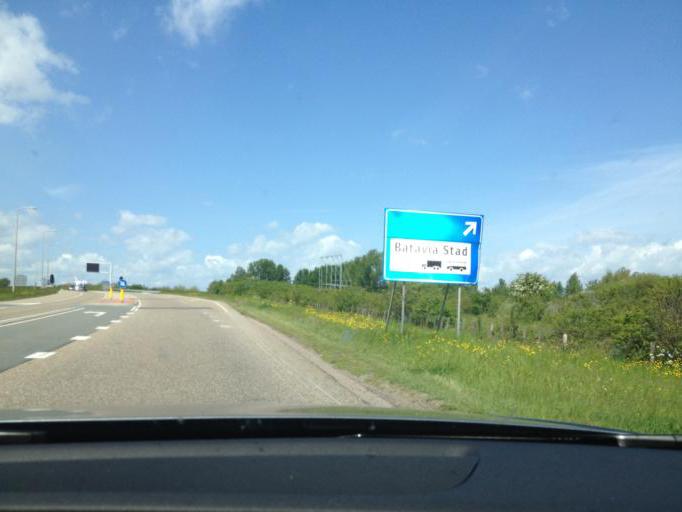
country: NL
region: Flevoland
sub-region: Gemeente Lelystad
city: Lelystad
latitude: 52.5266
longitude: 5.4402
